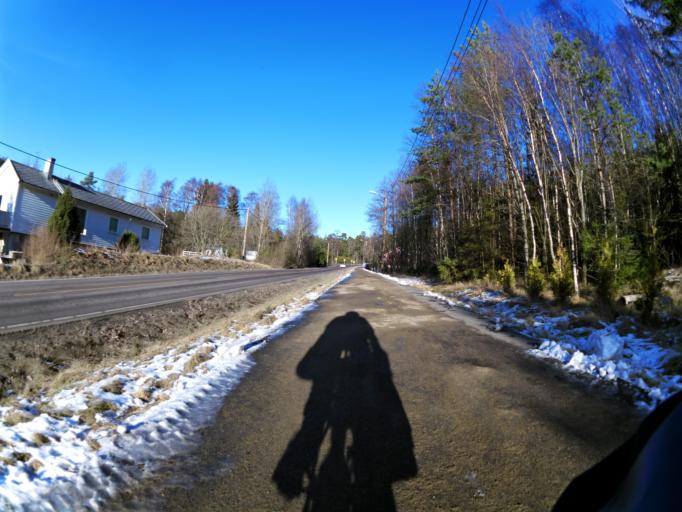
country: NO
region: Ostfold
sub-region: Fredrikstad
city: Fredrikstad
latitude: 59.1980
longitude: 10.8653
